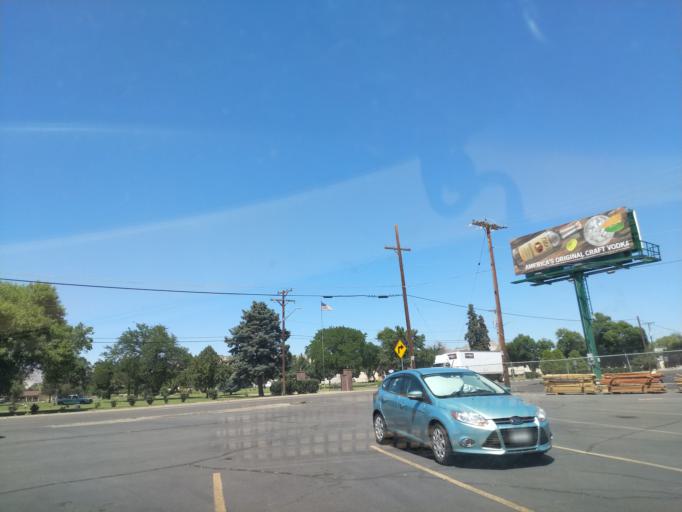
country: US
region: Colorado
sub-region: Mesa County
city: Fruitvale
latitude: 39.0770
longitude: -108.5029
